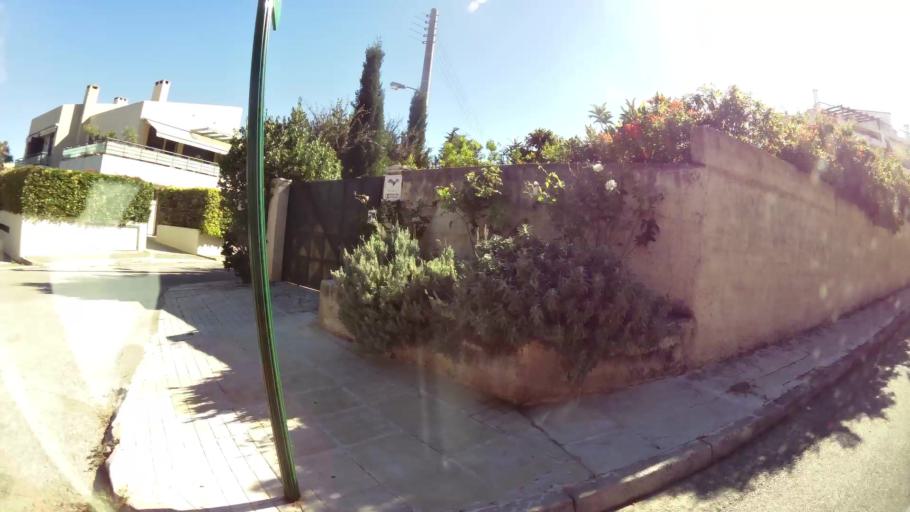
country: GR
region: Attica
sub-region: Nomarchia Anatolikis Attikis
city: Leondarion
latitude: 37.9869
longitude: 23.8610
